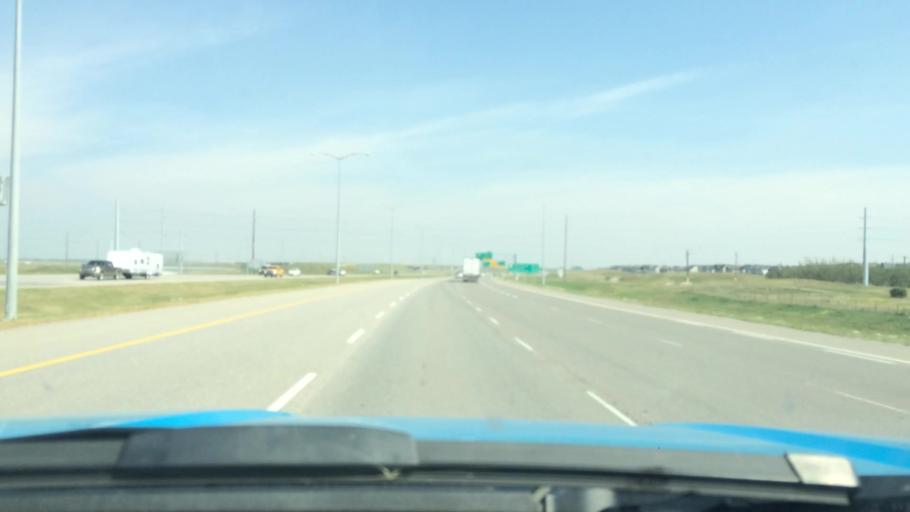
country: CA
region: Alberta
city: Chestermere
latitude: 50.9067
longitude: -113.9333
